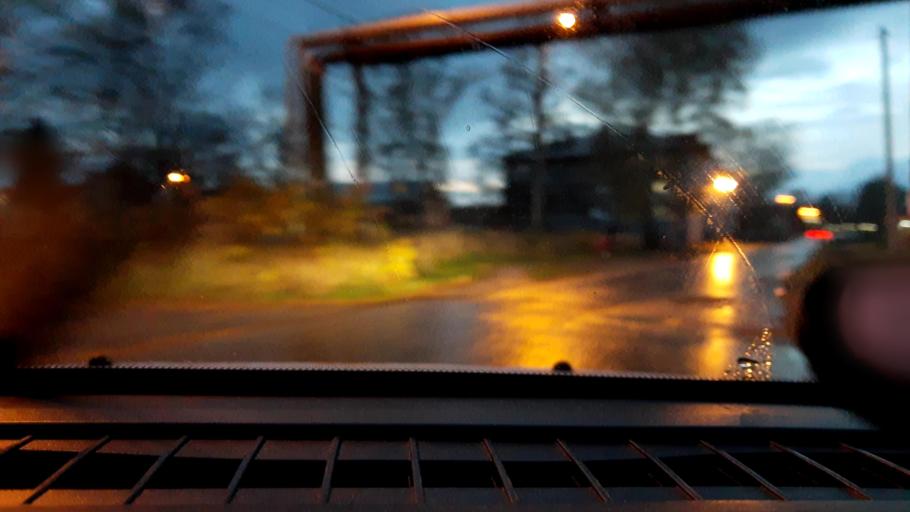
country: RU
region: Nizjnij Novgorod
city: Afonino
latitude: 56.2065
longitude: 44.1096
